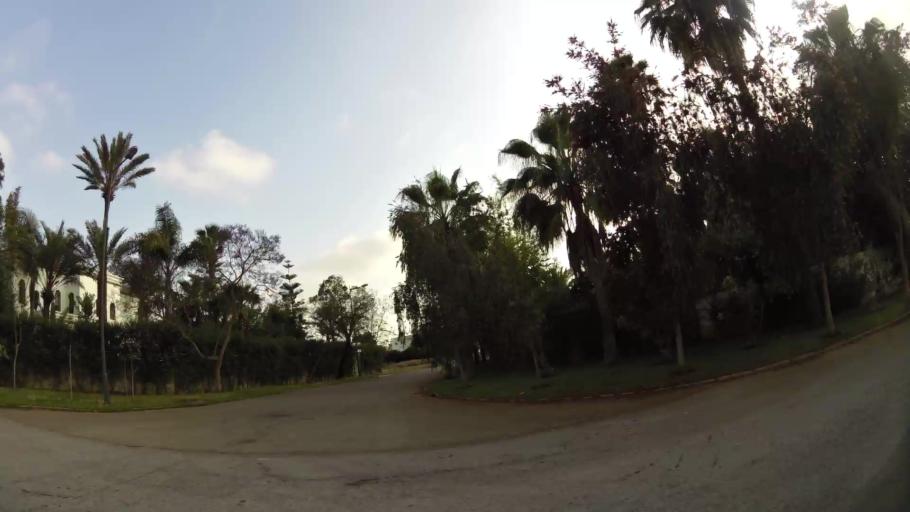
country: MA
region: Rabat-Sale-Zemmour-Zaer
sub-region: Rabat
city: Rabat
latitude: 33.9471
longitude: -6.8166
